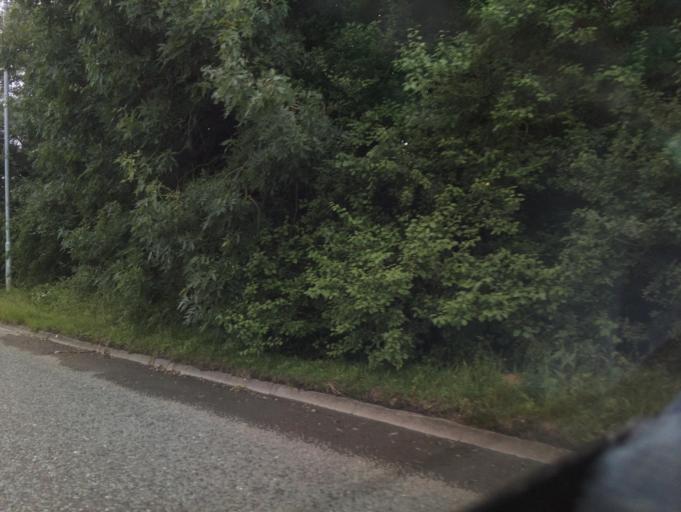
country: GB
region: England
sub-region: Northamptonshire
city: Geddington
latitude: 52.4601
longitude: -0.7375
